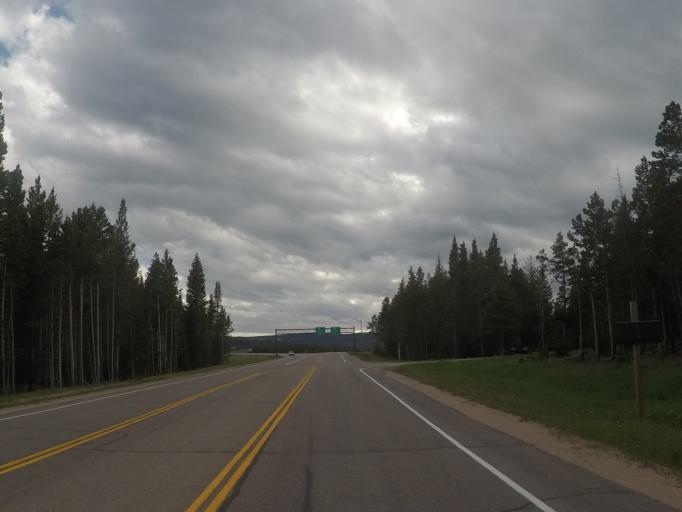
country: US
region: Wyoming
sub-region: Sheridan County
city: Sheridan
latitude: 44.7744
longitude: -107.5145
